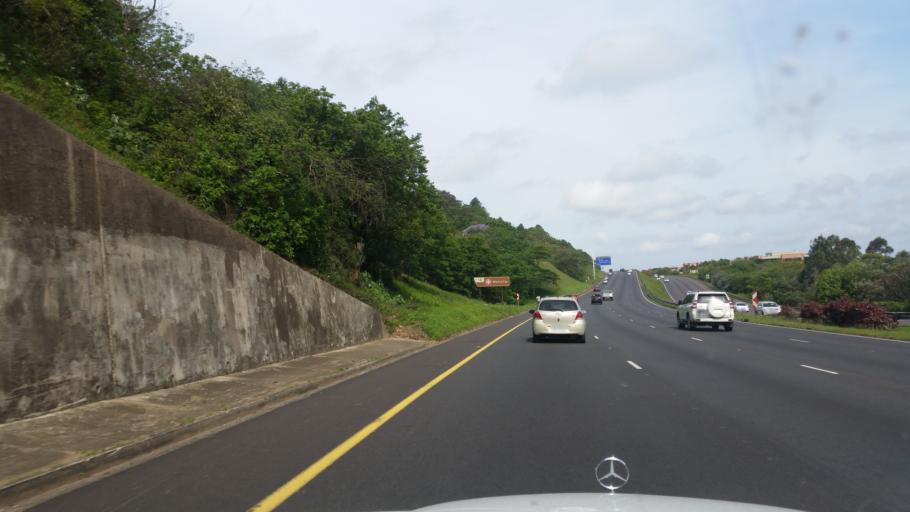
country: ZA
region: KwaZulu-Natal
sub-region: eThekwini Metropolitan Municipality
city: Berea
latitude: -29.8423
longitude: 30.9191
